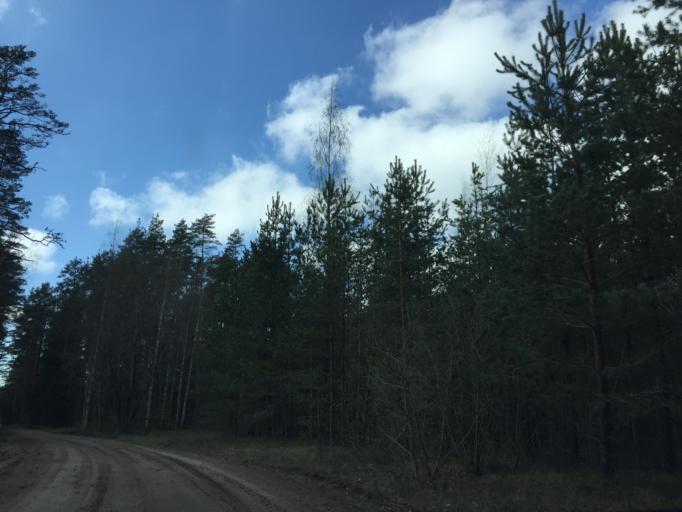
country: EE
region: Valgamaa
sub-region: Valga linn
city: Valga
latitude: 57.6133
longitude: 26.1772
